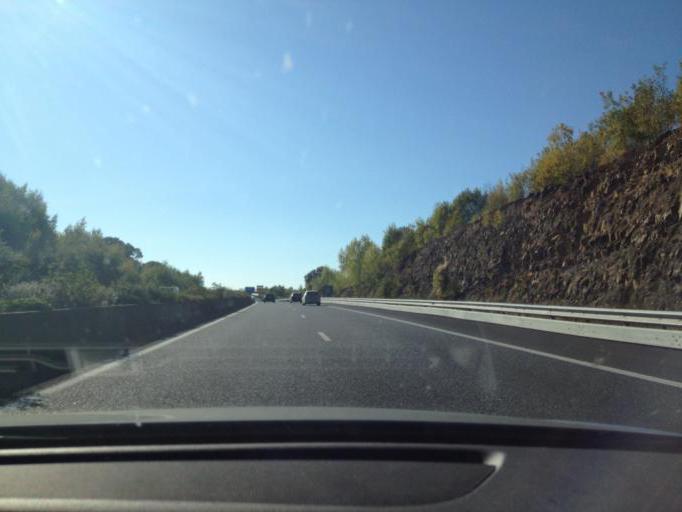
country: LU
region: Grevenmacher
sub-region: Canton de Remich
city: Dalheim
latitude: 49.5190
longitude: 6.2562
